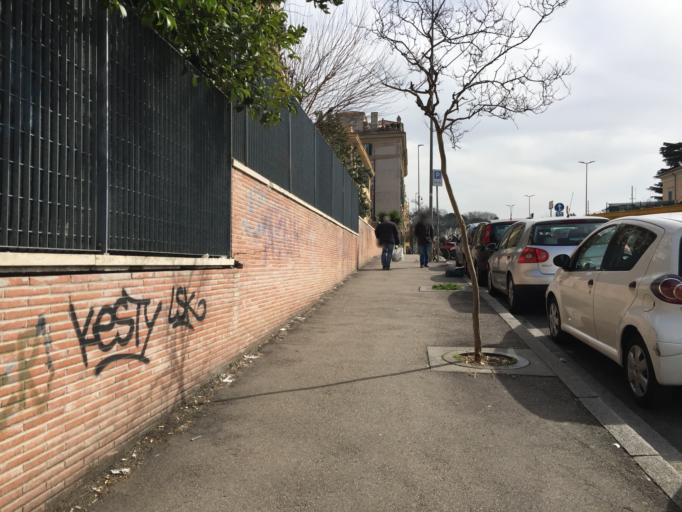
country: VA
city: Vatican City
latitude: 41.8971
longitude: 12.4544
